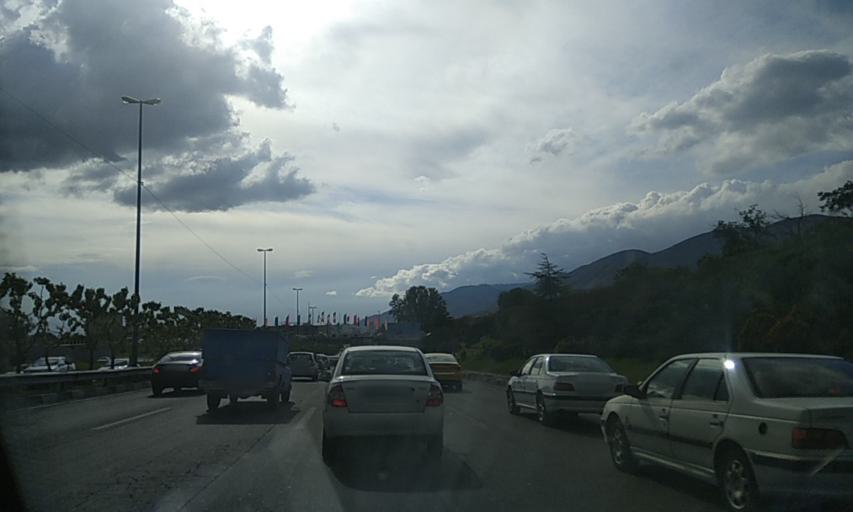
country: IR
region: Tehran
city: Tehran
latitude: 35.7539
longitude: 51.2818
